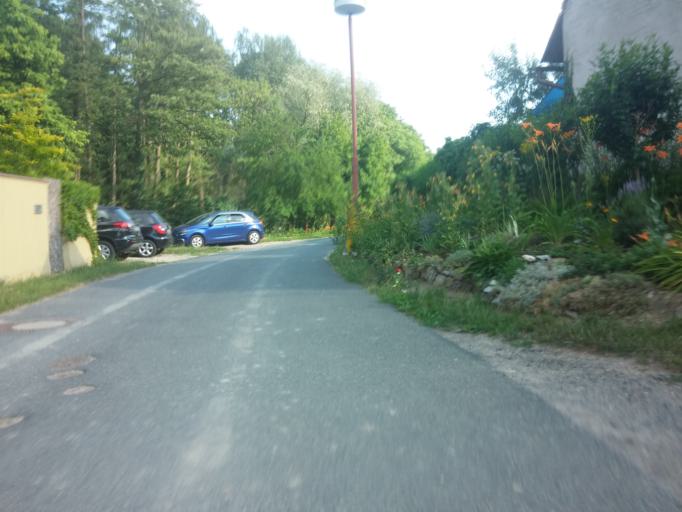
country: CZ
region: Central Bohemia
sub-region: Okres Nymburk
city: Podebrady
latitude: 50.1298
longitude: 15.1144
